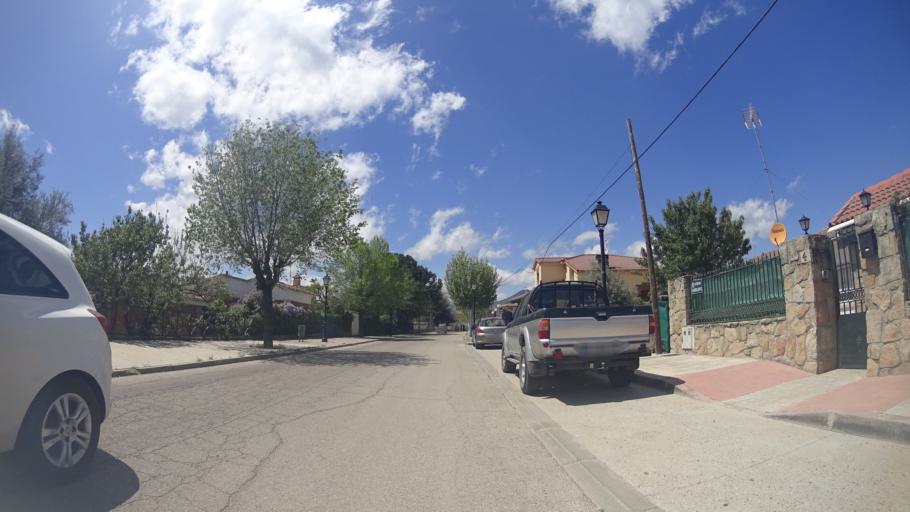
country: ES
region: Madrid
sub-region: Provincia de Madrid
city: San Martin de Valdeiglesias
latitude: 40.3655
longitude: -4.3945
